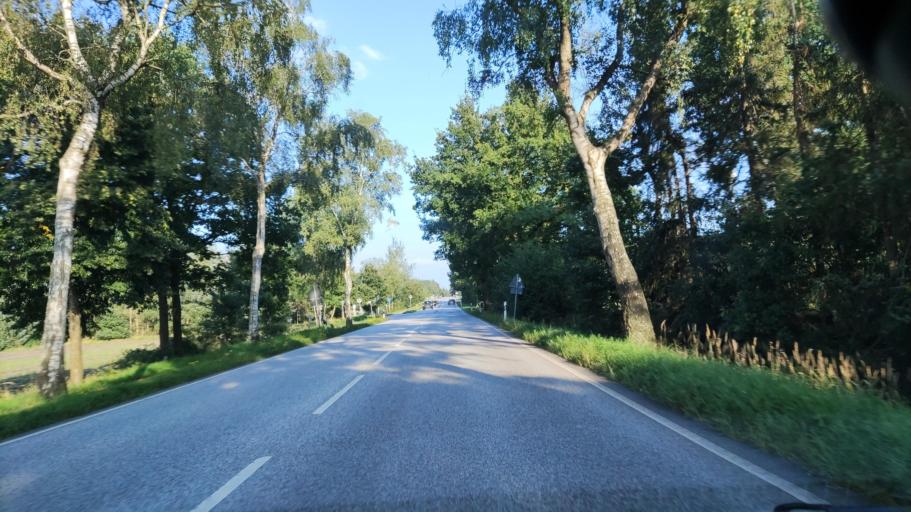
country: DE
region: Schleswig-Holstein
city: Bimohlen
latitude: 53.9045
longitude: 9.9299
